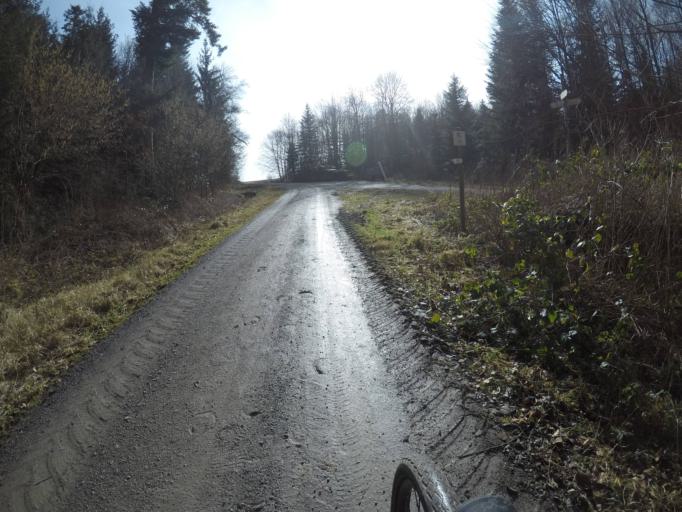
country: DE
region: Baden-Wuerttemberg
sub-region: Regierungsbezirk Stuttgart
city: Oberjettingen
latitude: 48.5885
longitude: 8.7945
